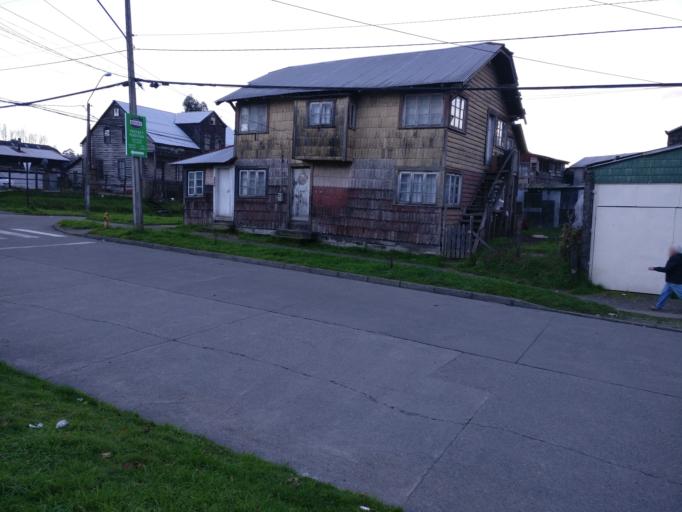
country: CL
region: Los Lagos
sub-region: Provincia de Llanquihue
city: Puerto Varas
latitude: -41.3157
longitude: -72.9902
